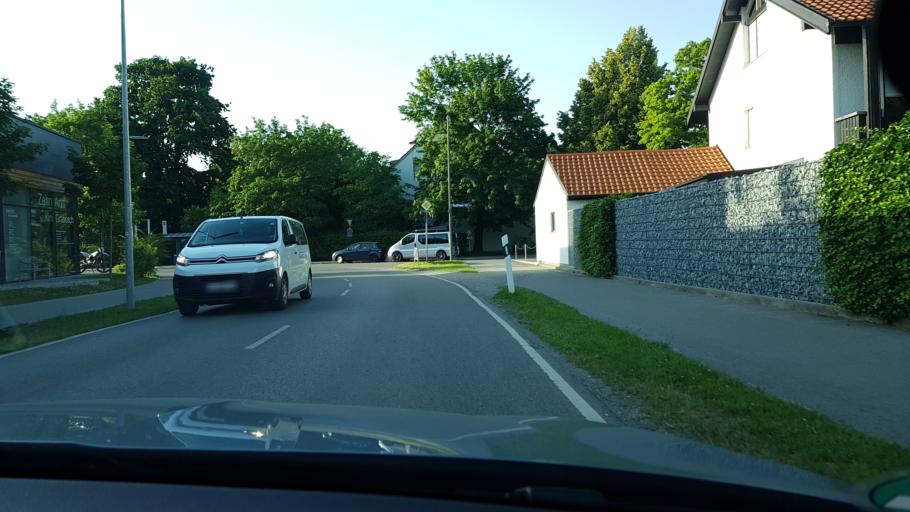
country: DE
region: Bavaria
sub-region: Upper Bavaria
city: Bogenhausen
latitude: 48.1490
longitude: 11.6582
